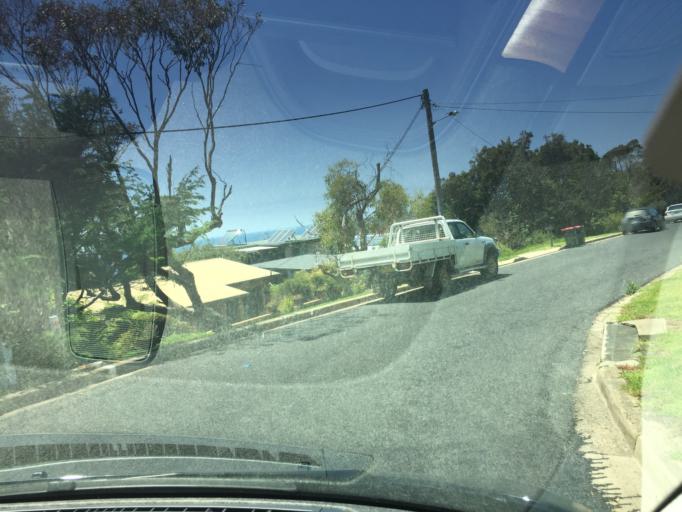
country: AU
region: New South Wales
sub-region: Bega Valley
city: Bega
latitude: -36.7327
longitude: 149.9846
